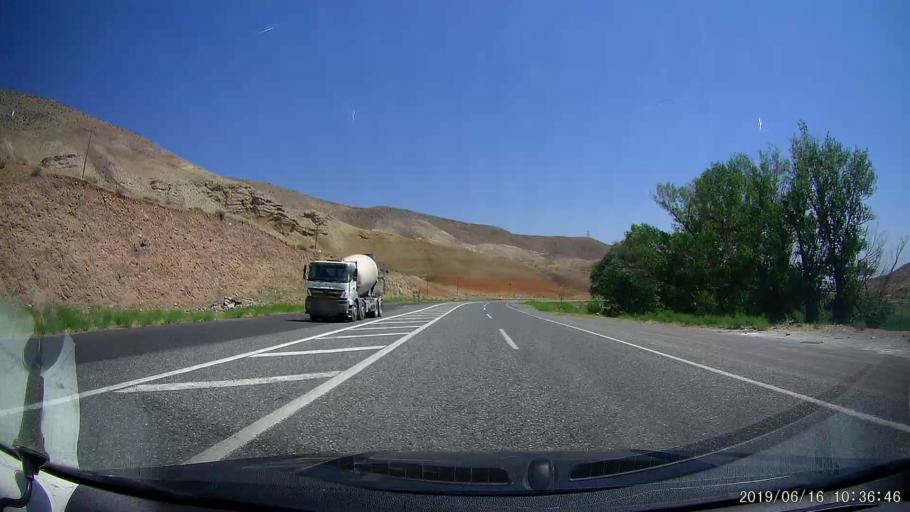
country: TR
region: Igdir
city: Tuzluca
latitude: 40.0418
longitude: 43.6867
